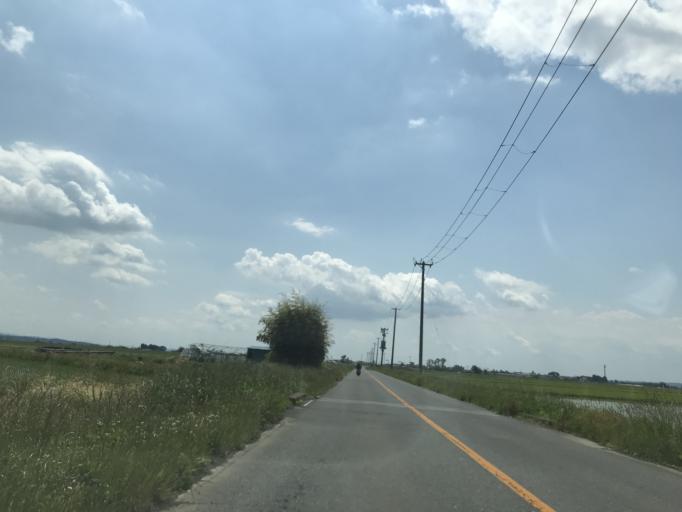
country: JP
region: Miyagi
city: Kogota
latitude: 38.5935
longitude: 141.0278
